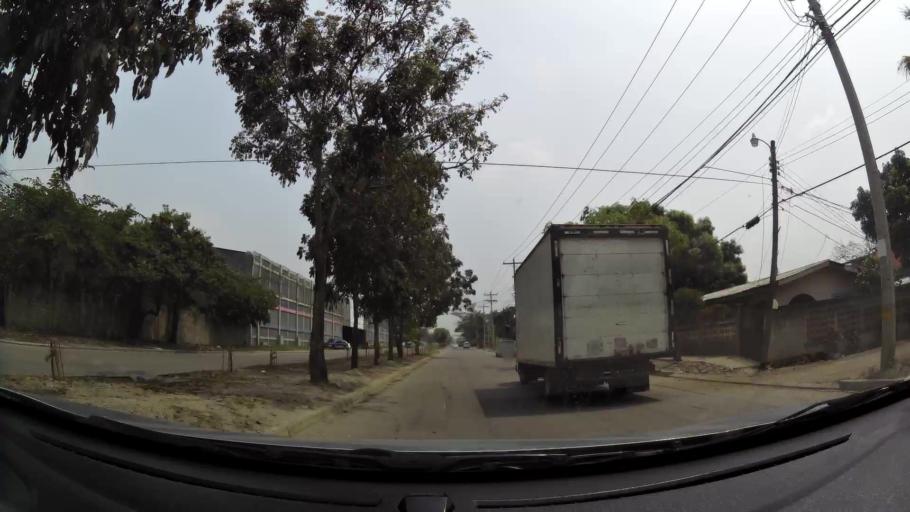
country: HN
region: Cortes
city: San Pedro Sula
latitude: 15.4811
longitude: -88.0254
